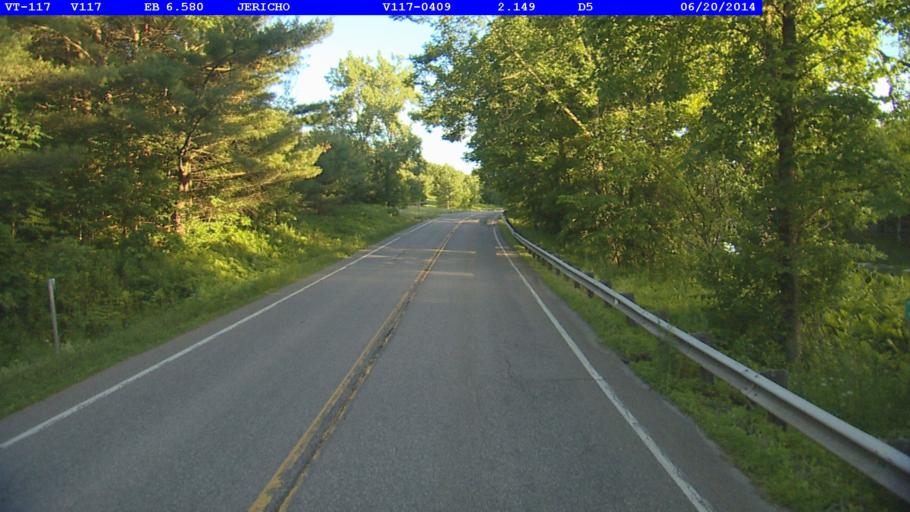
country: US
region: Vermont
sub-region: Chittenden County
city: Williston
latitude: 44.4445
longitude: -73.0190
